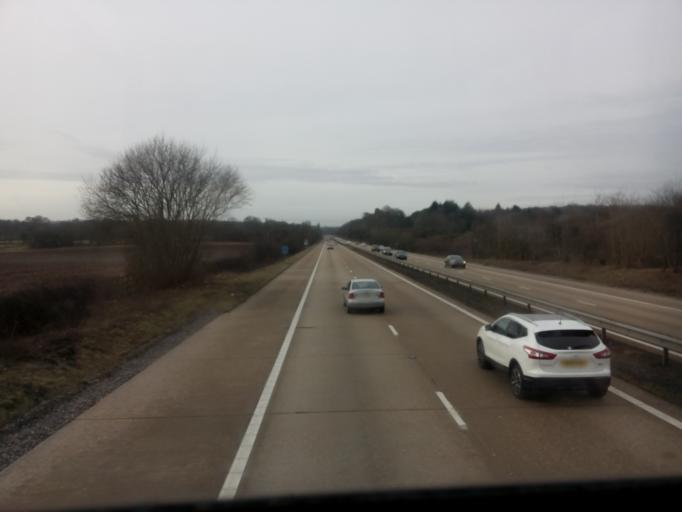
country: GB
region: England
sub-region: Hampshire
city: Overton
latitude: 51.1823
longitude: -1.2146
